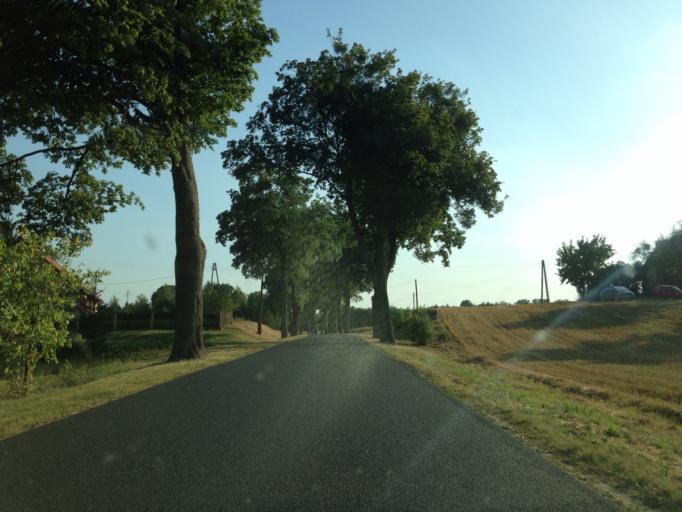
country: PL
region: Kujawsko-Pomorskie
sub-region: Powiat brodnicki
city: Brodnica
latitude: 53.3479
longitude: 19.3761
